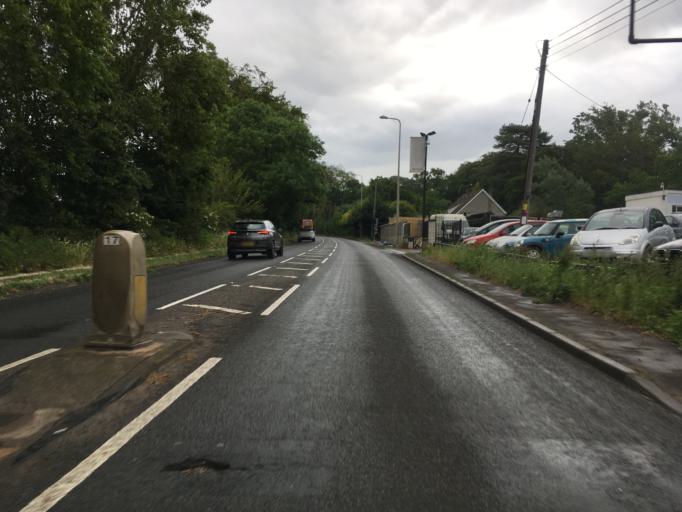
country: GB
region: England
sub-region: North Somerset
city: Brockley
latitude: 51.3876
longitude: -2.7813
